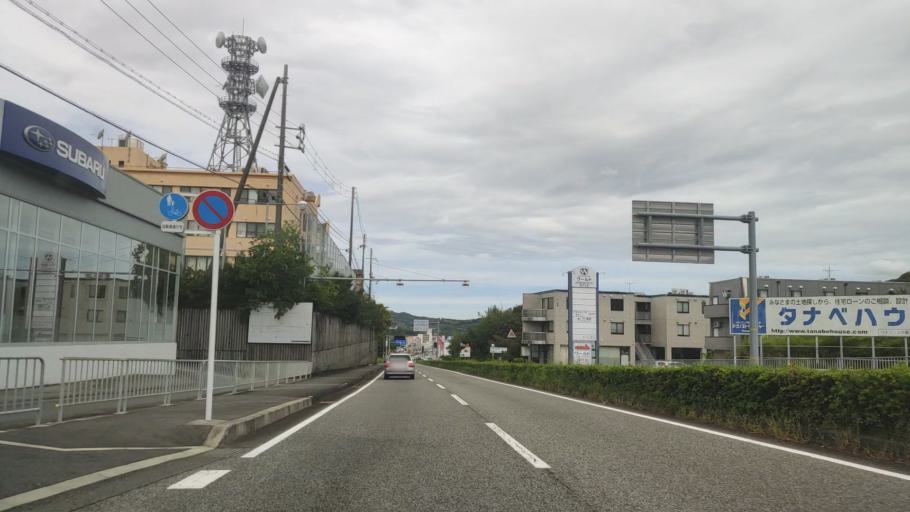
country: JP
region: Wakayama
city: Tanabe
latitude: 33.7359
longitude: 135.3993
